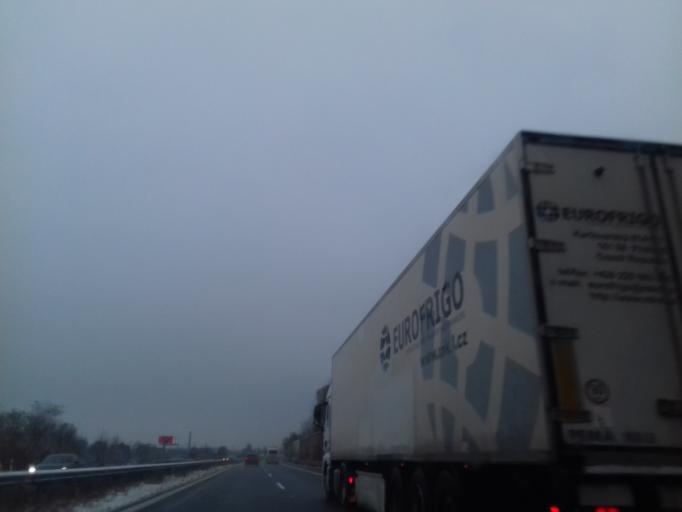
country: CZ
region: Central Bohemia
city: Zdice
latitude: 49.9158
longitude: 13.9954
